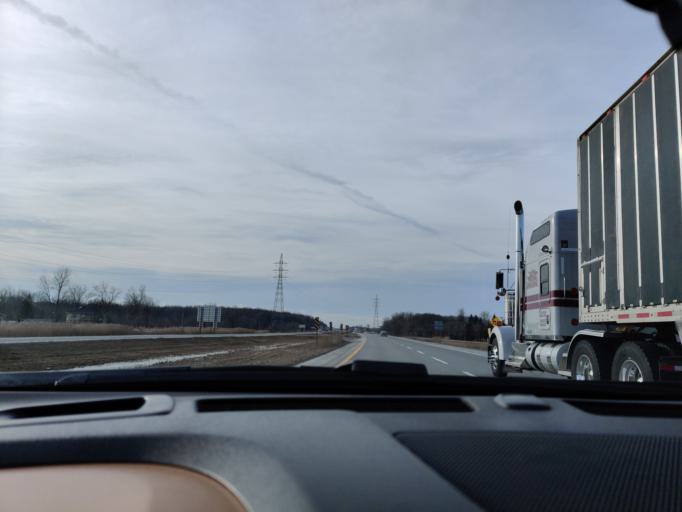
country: CA
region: Quebec
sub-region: Monteregie
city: Les Coteaux
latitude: 45.2967
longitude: -74.1860
